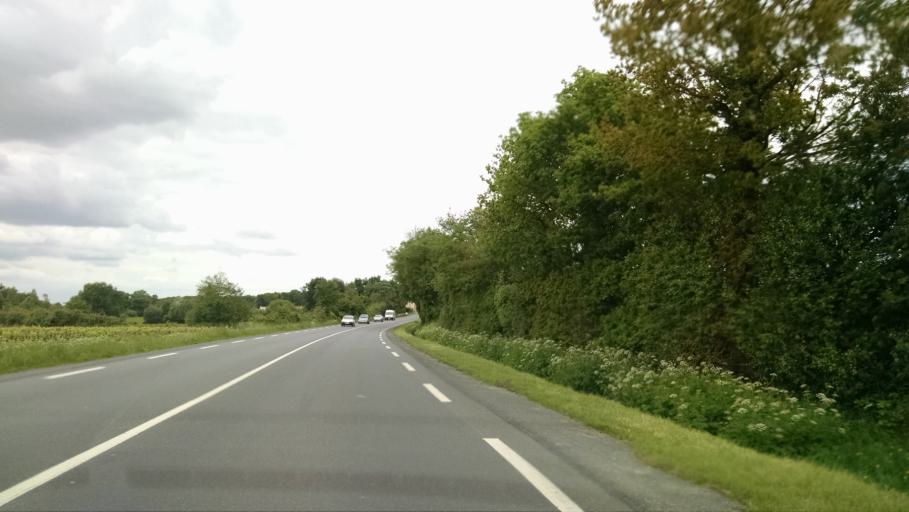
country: FR
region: Pays de la Loire
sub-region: Departement de la Loire-Atlantique
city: Le Bignon
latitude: 47.1062
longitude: -1.4684
